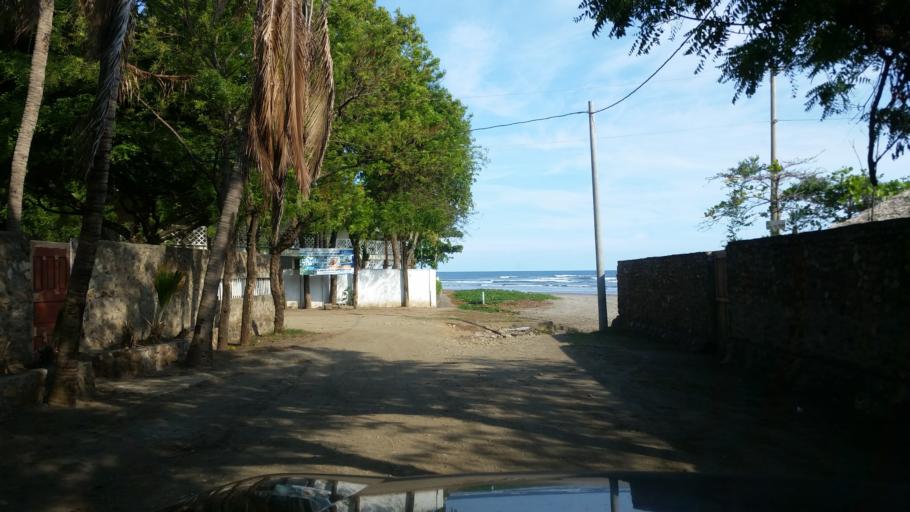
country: NI
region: Managua
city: Masachapa
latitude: 11.7748
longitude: -86.5132
